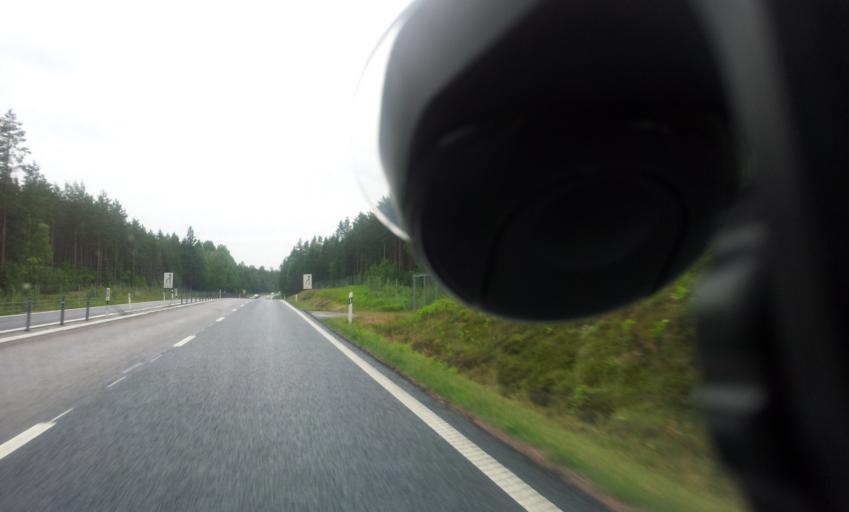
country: SE
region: Kalmar
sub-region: Monsteras Kommun
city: Timmernabben
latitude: 56.8752
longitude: 16.3825
